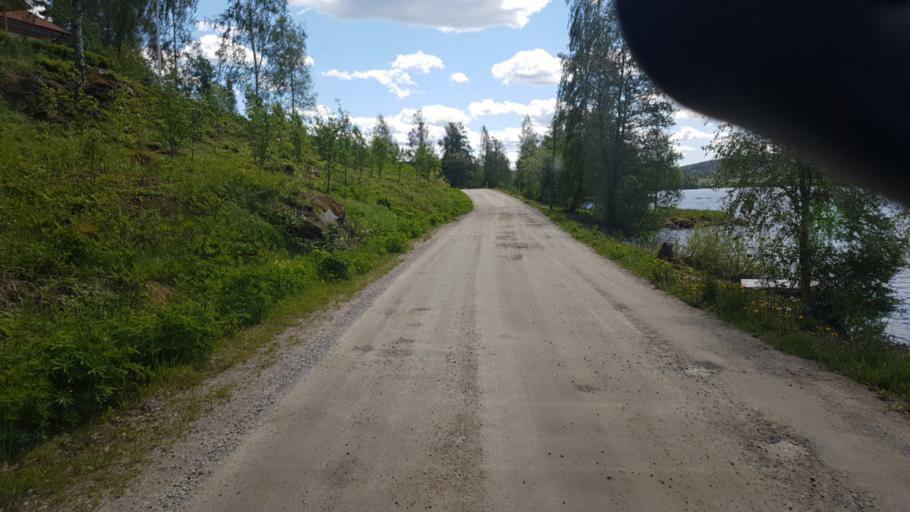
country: SE
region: Vaermland
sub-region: Arvika Kommun
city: Arvika
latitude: 59.7256
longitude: 12.8365
